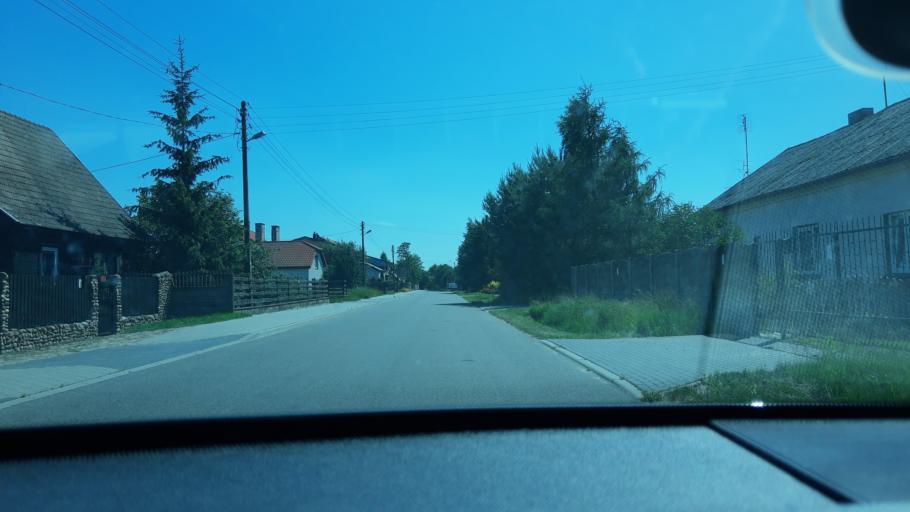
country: PL
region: Lodz Voivodeship
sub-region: Powiat zdunskowolski
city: Zdunska Wola
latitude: 51.6031
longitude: 18.9844
